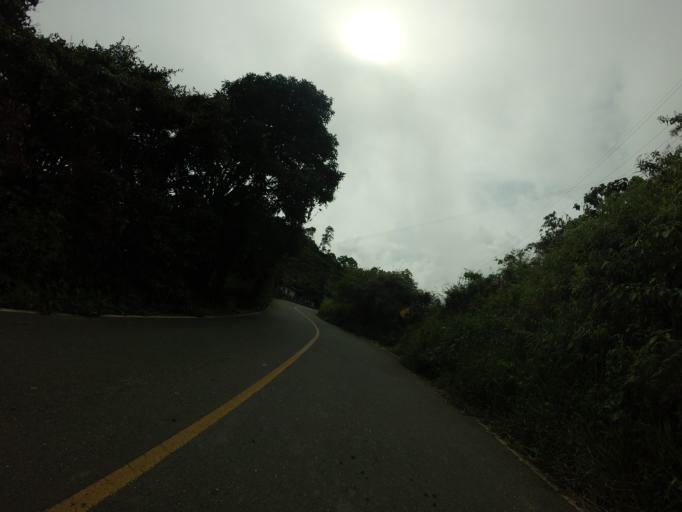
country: CO
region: Caldas
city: Marquetalia
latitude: 5.2987
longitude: -75.0334
